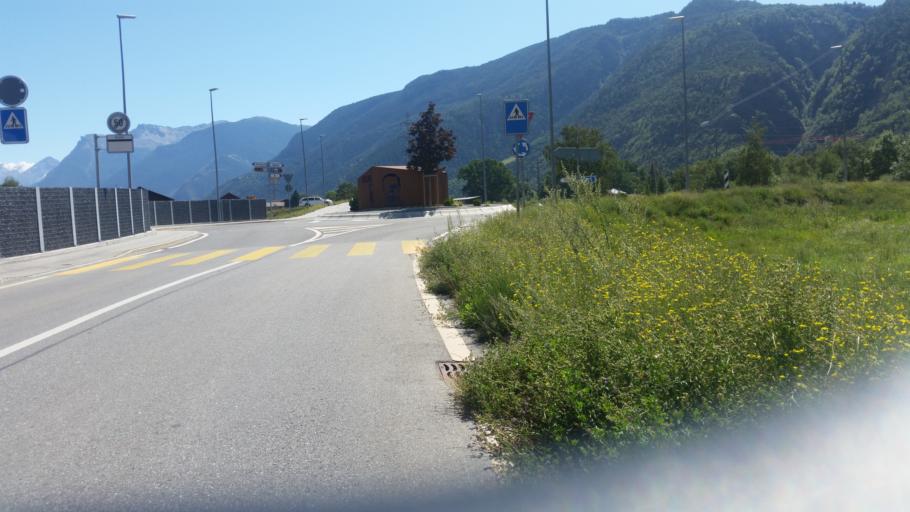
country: CH
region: Valais
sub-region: Raron District
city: Raron
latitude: 46.3102
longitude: 7.7917
